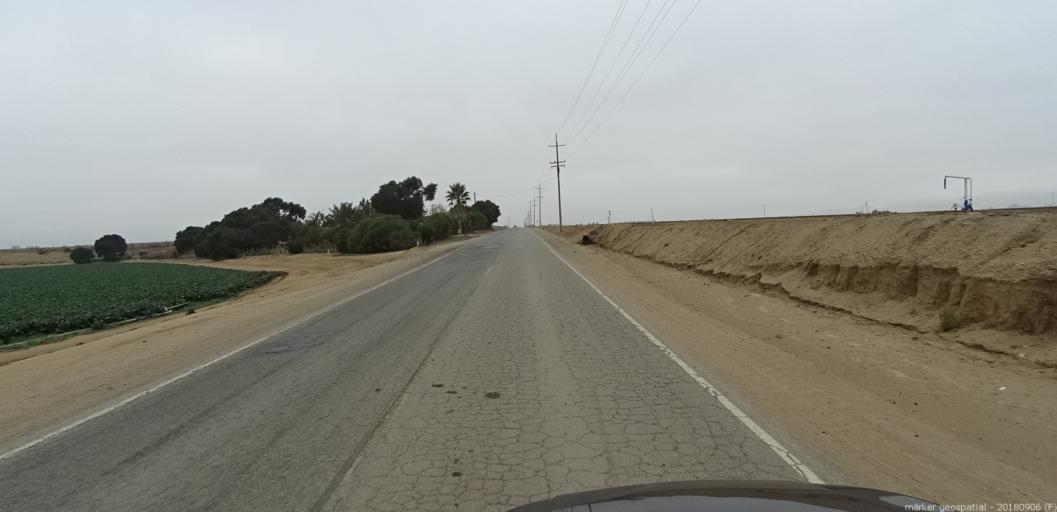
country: US
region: California
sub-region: Monterey County
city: Salinas
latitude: 36.6624
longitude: -121.5919
